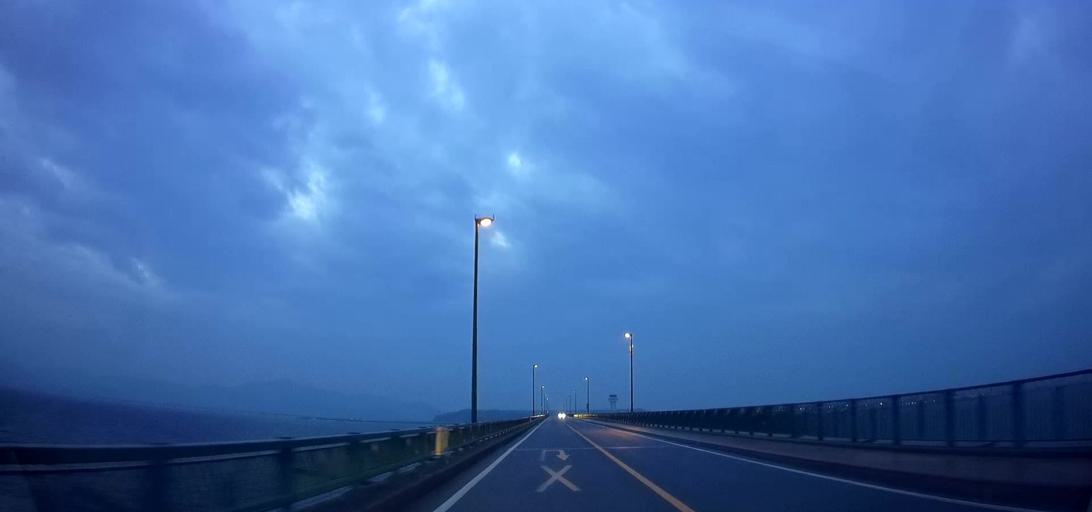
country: JP
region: Nagasaki
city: Omura
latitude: 32.9183
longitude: 129.9335
